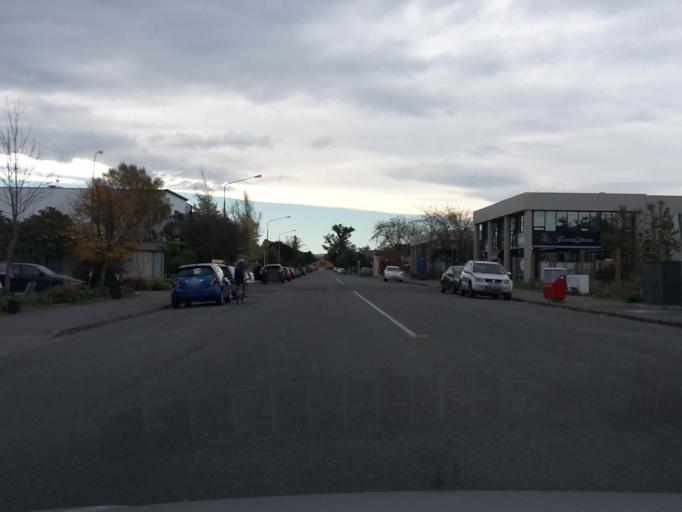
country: NZ
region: Canterbury
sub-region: Christchurch City
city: Christchurch
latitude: -43.5340
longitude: 172.6067
